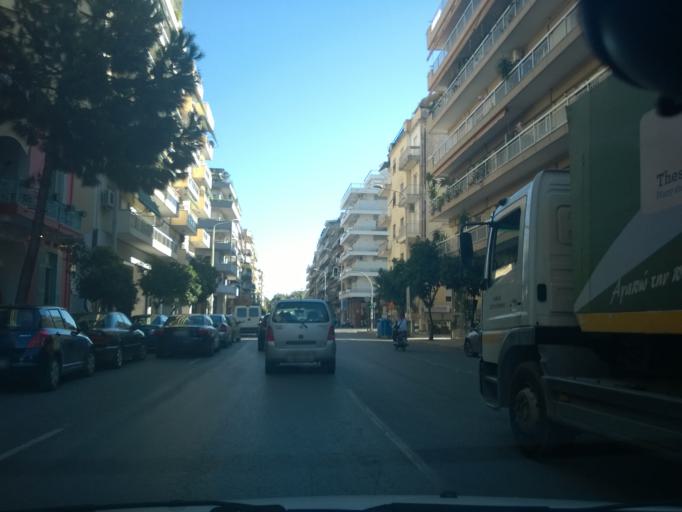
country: GR
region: Central Macedonia
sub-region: Nomos Thessalonikis
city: Kalamaria
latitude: 40.5993
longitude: 22.9517
